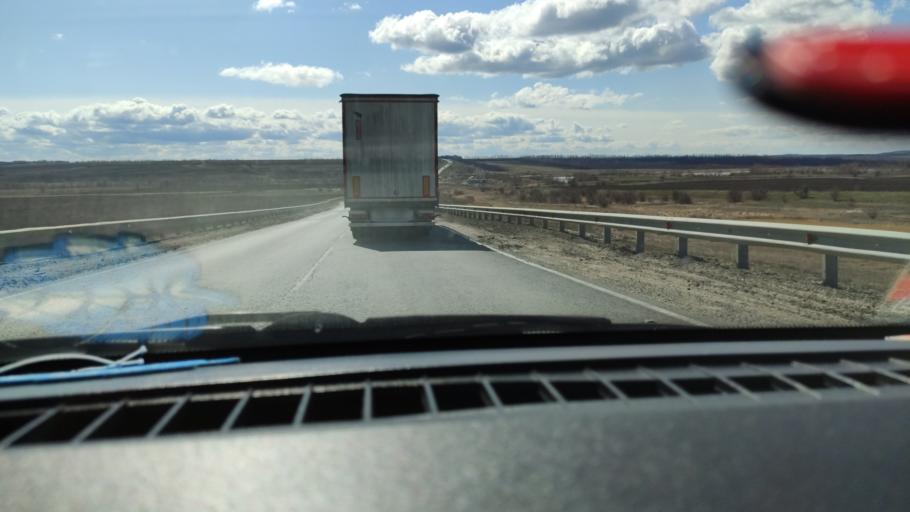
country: RU
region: Saratov
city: Dukhovnitskoye
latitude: 52.7450
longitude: 48.2519
